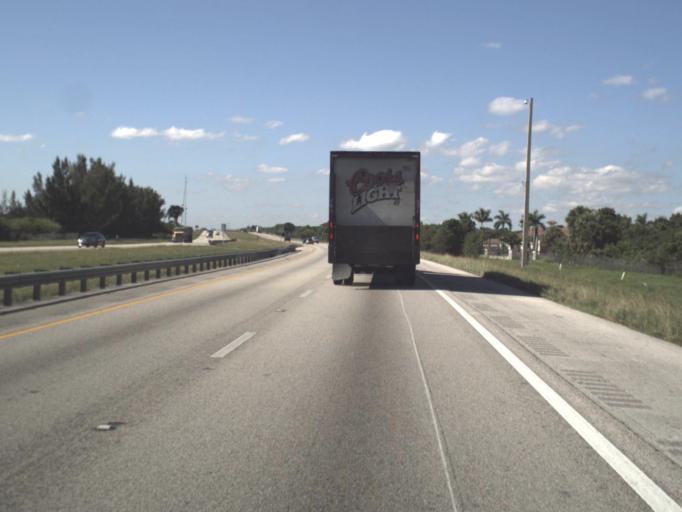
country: US
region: Florida
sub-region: Miami-Dade County
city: Country Club
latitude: 25.9685
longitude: -80.3271
